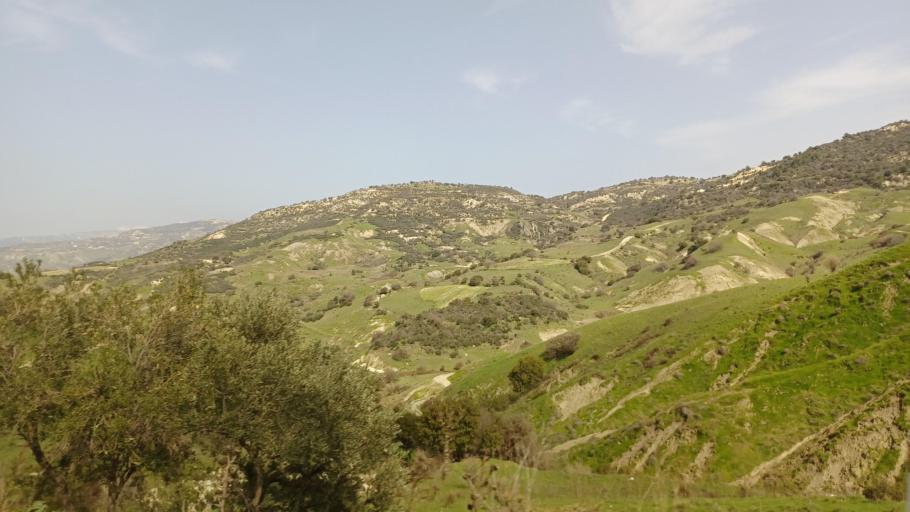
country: CY
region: Limassol
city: Pissouri
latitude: 34.7490
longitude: 32.6607
